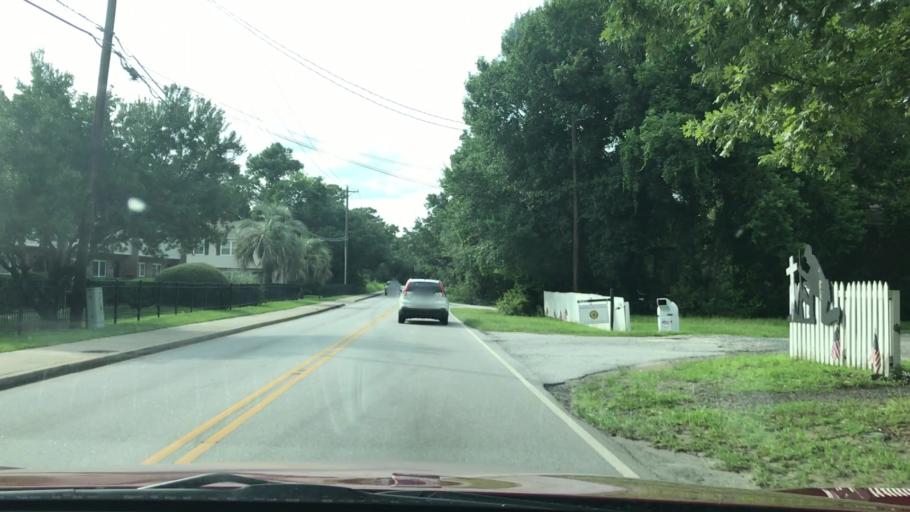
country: US
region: South Carolina
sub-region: Charleston County
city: North Charleston
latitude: 32.8122
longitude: -80.0122
